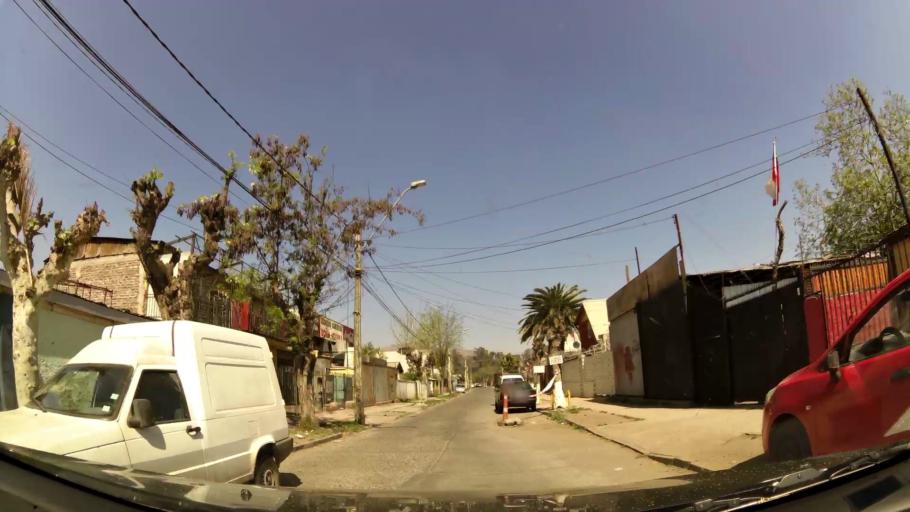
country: CL
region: Santiago Metropolitan
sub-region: Provincia de Santiago
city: Lo Prado
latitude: -33.3674
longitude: -70.7388
